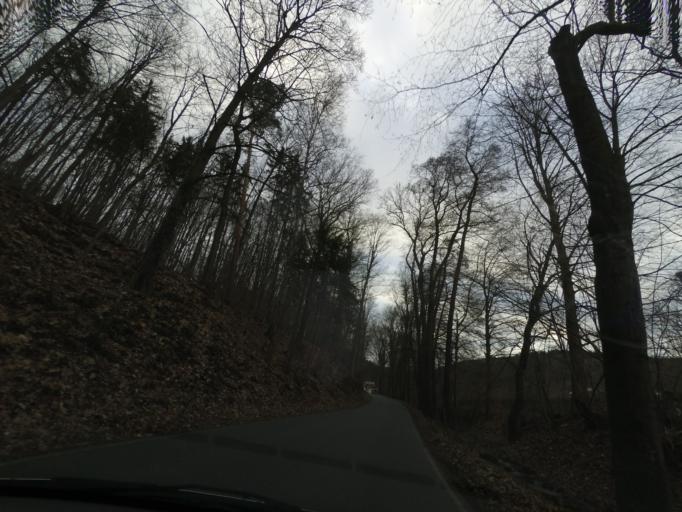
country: DE
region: Thuringia
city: Saalfeld
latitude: 50.6370
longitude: 11.3451
